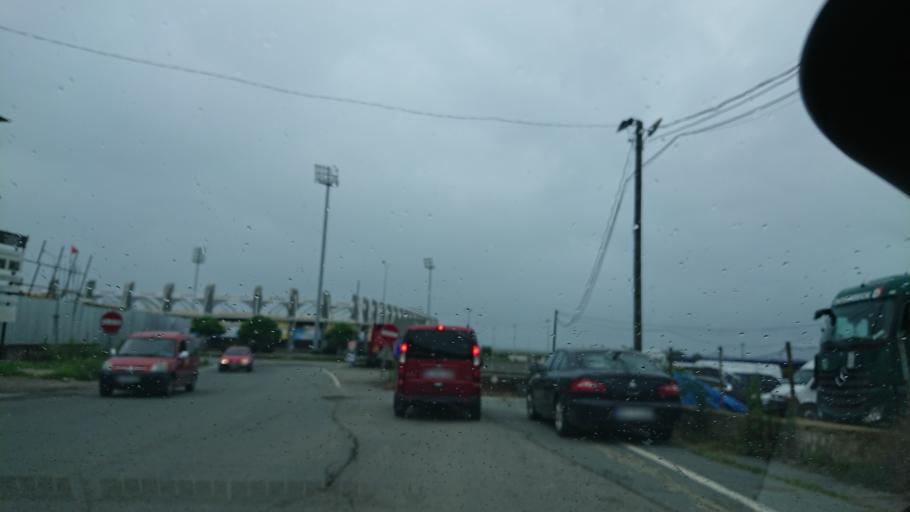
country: TR
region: Rize
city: Gundogdu
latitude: 41.0407
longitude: 40.5752
